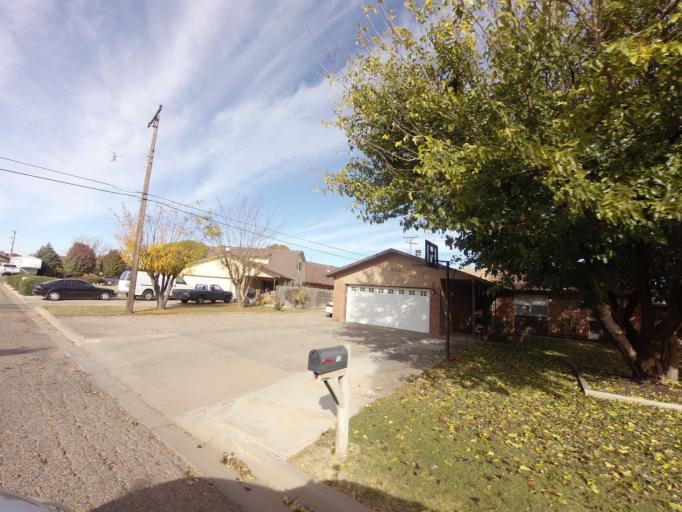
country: US
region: New Mexico
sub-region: Curry County
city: Clovis
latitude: 34.4203
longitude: -103.2285
